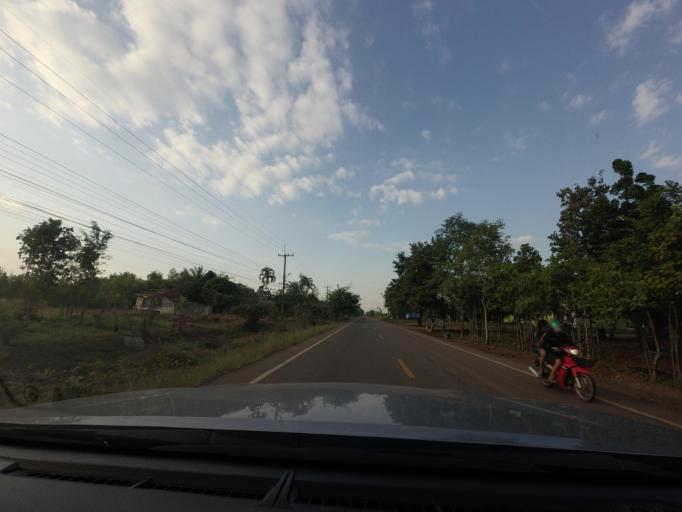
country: TH
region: Phitsanulok
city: Noen Maprang
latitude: 16.5972
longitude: 100.6242
